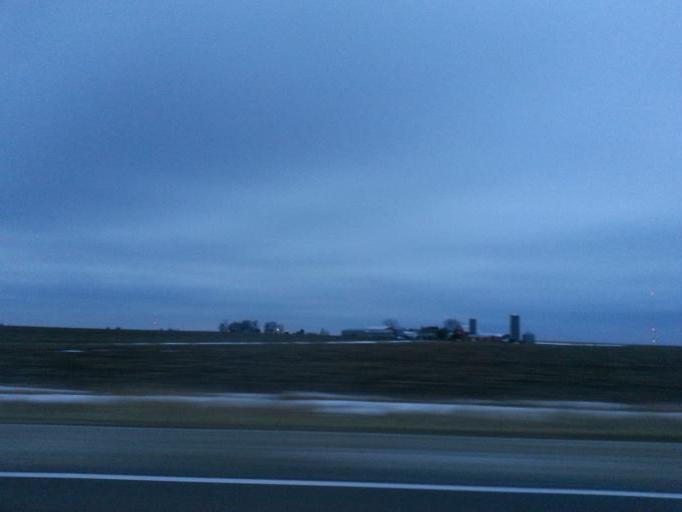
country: US
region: Iowa
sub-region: Black Hawk County
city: La Porte City
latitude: 42.3919
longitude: -92.1369
